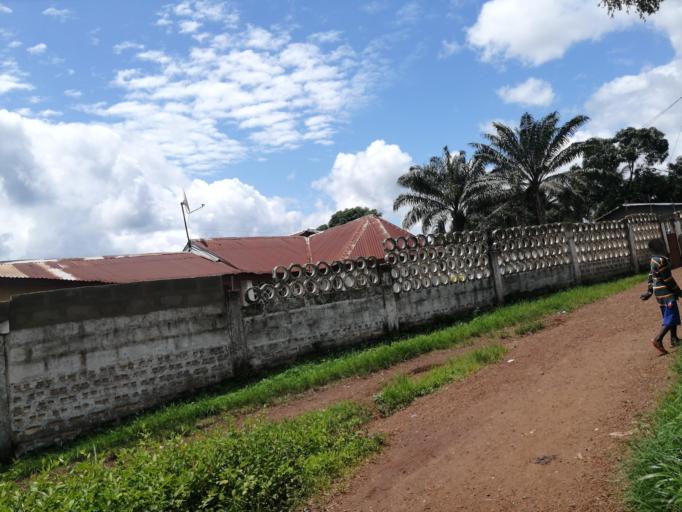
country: SL
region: Northern Province
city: Port Loko
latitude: 8.7688
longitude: -12.7834
